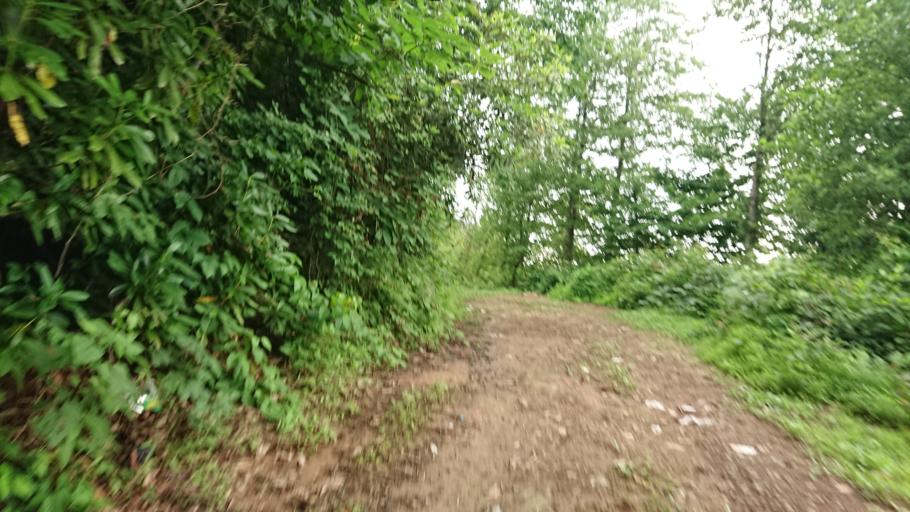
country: TR
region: Rize
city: Rize
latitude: 40.9877
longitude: 40.5055
